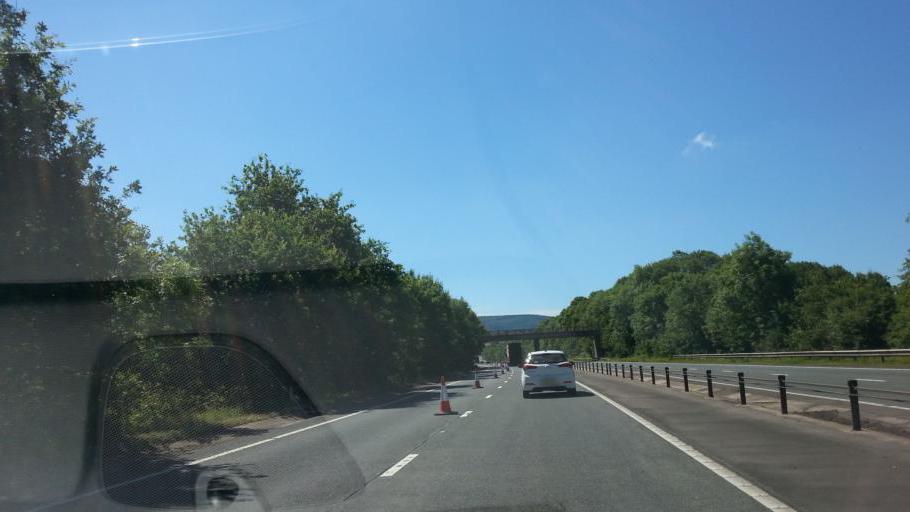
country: GB
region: Wales
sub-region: Monmouthshire
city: Llanbadoc
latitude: 51.6904
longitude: -2.8792
